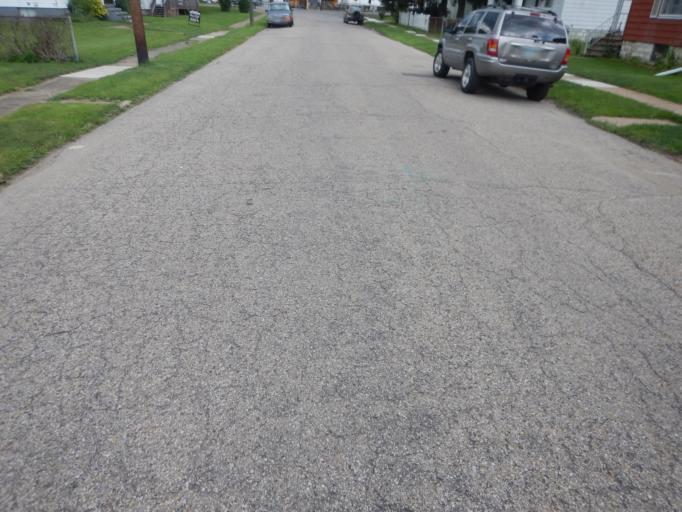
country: US
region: Ohio
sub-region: Muskingum County
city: North Zanesville
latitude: 39.9662
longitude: -81.9981
